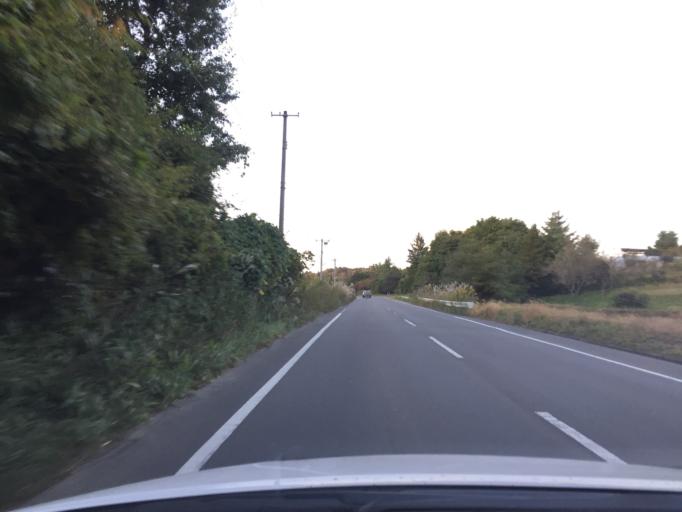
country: JP
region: Fukushima
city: Koriyama
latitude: 37.3541
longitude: 140.4468
